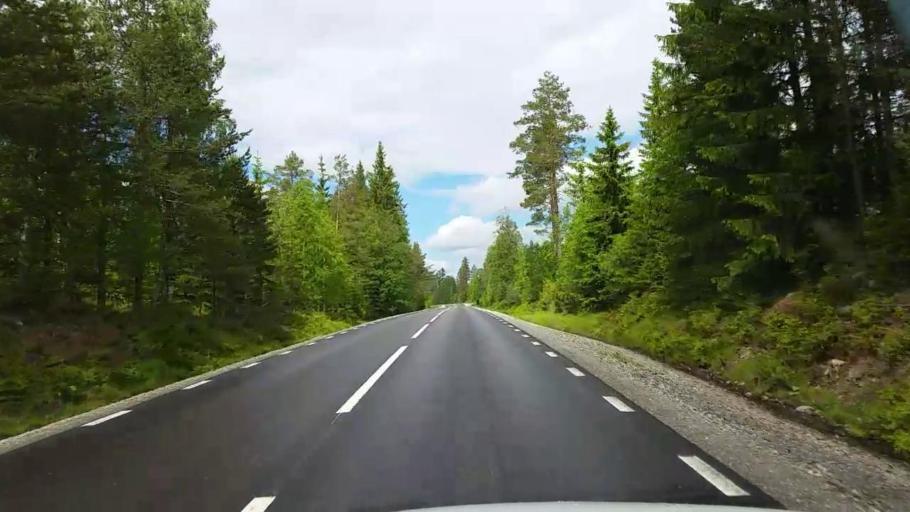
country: SE
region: Gaevleborg
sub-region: Sandvikens Kommun
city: Jarbo
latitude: 60.8837
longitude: 16.3842
